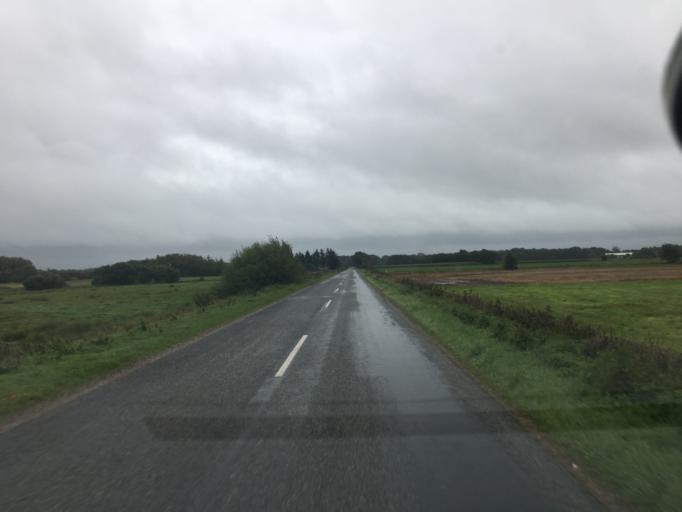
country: DE
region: Schleswig-Holstein
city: Bramstedtlund
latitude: 54.9669
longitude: 9.0472
